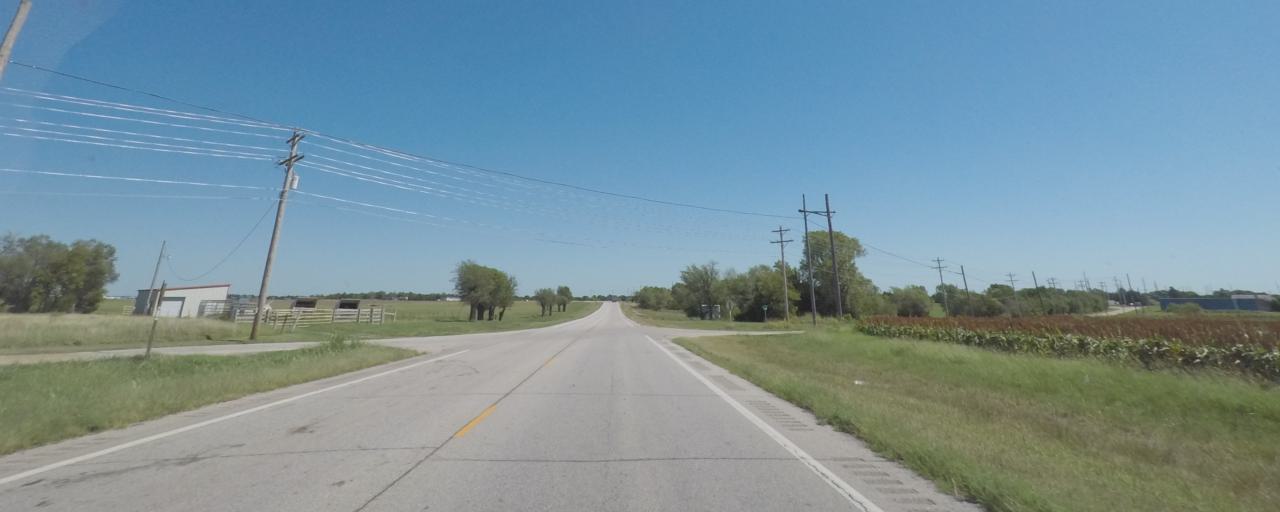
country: US
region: Kansas
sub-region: Sumner County
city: Wellington
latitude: 37.3038
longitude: -97.3897
